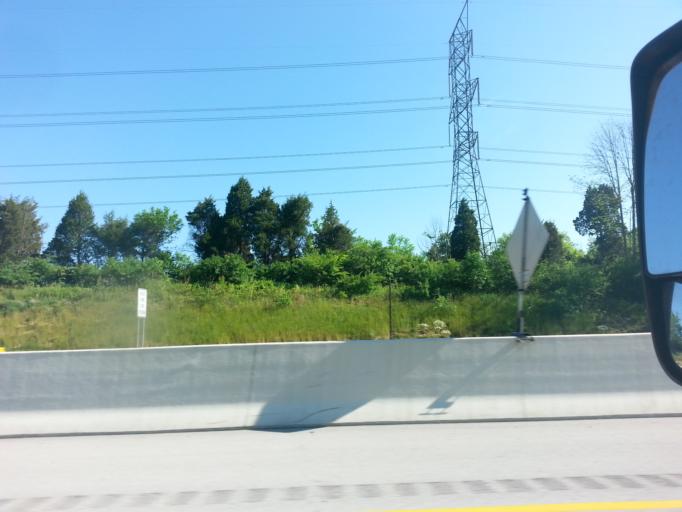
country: US
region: Kentucky
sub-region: Jefferson County
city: Middletown
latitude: 38.2222
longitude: -85.4905
